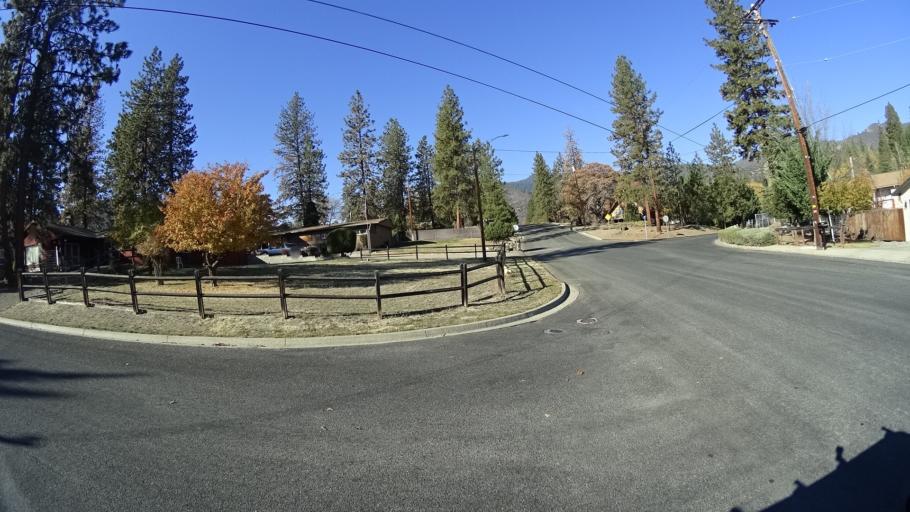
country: US
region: California
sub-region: Siskiyou County
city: Yreka
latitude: 41.7353
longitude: -122.6533
